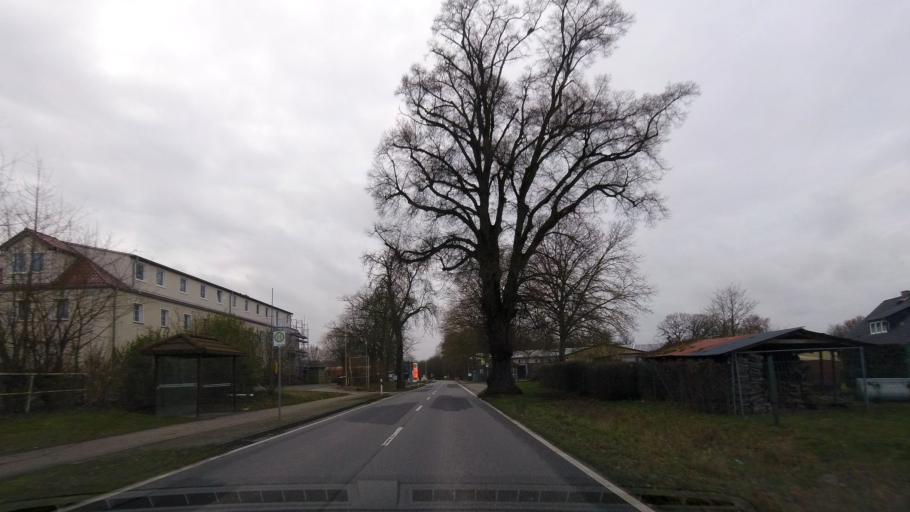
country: DE
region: Mecklenburg-Vorpommern
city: Robel
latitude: 53.3619
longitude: 12.4990
